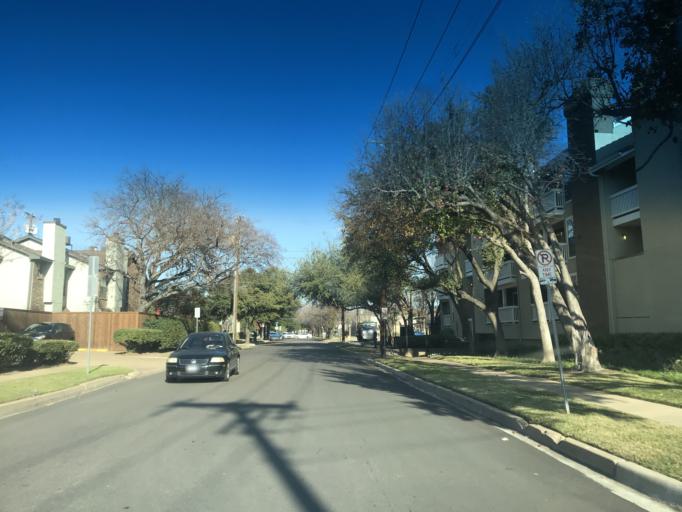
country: US
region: Texas
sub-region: Dallas County
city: Highland Park
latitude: 32.8118
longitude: -96.8080
